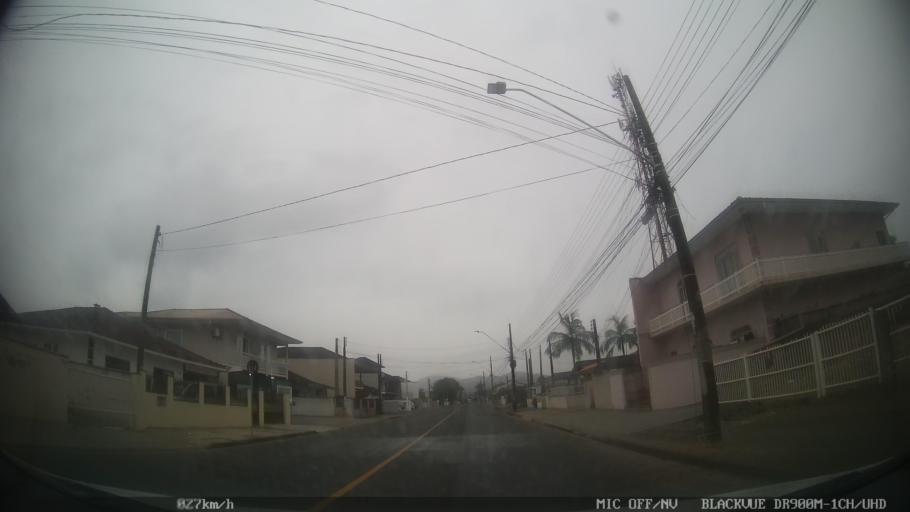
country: BR
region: Santa Catarina
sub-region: Joinville
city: Joinville
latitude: -26.2695
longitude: -48.8022
